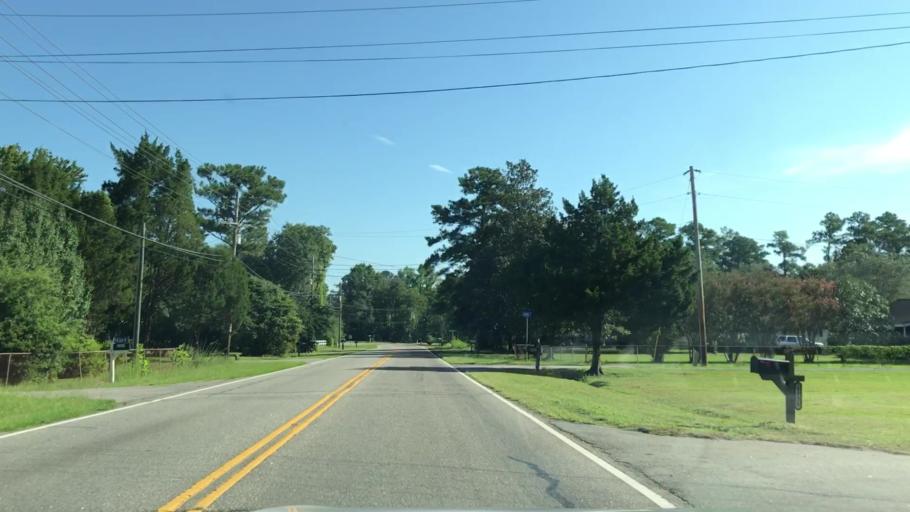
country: US
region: South Carolina
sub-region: Georgetown County
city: Georgetown
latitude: 33.4350
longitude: -79.2769
